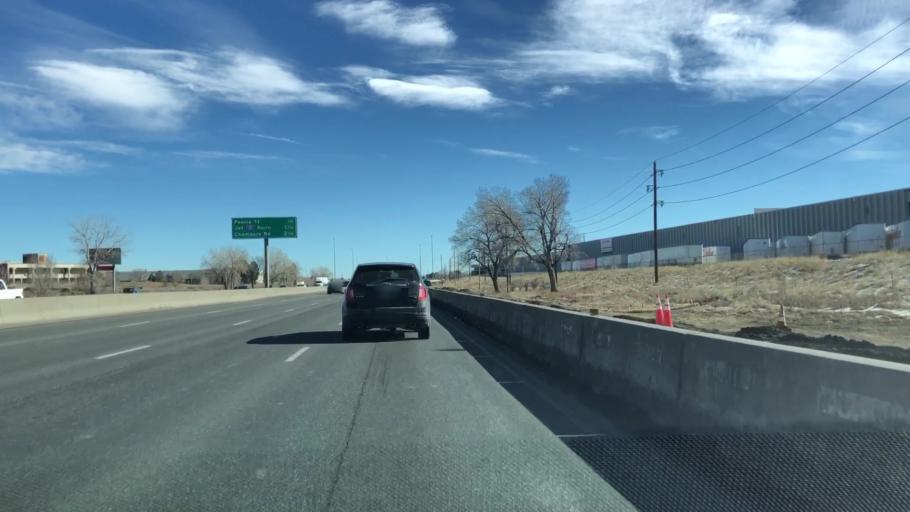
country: US
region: Colorado
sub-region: Adams County
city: Aurora
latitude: 39.7743
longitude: -104.8576
